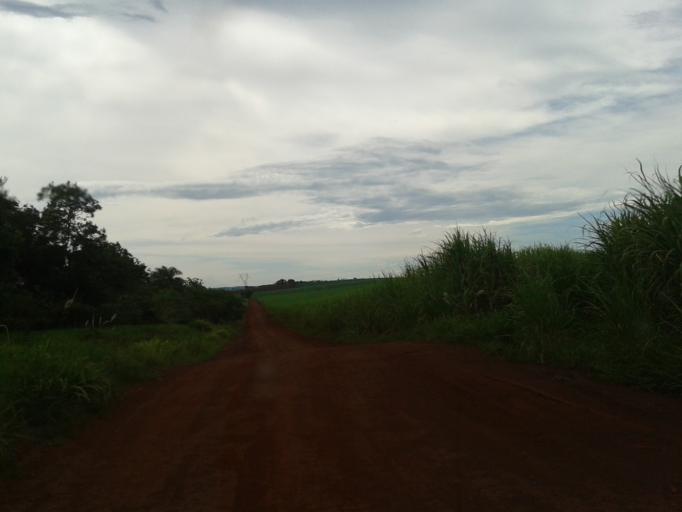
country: BR
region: Minas Gerais
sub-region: Centralina
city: Centralina
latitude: -18.6464
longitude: -49.3255
